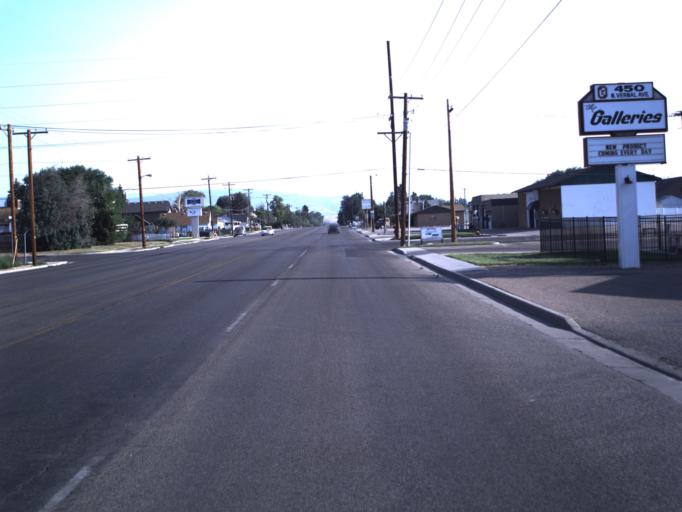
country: US
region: Utah
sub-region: Uintah County
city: Vernal
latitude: 40.4623
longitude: -109.5286
